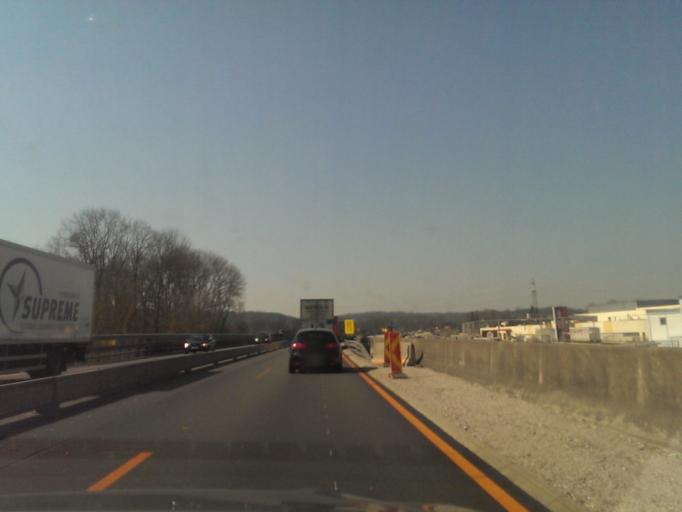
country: AT
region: Upper Austria
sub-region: Politischer Bezirk Vocklabruck
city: Wolfsegg am Hausruck
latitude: 48.1902
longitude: 13.6589
